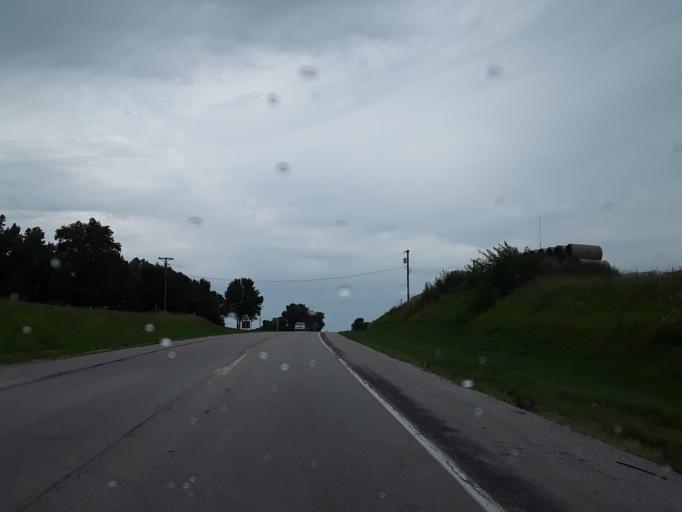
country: US
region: Nebraska
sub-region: Washington County
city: Blair
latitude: 41.5060
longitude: -96.1579
